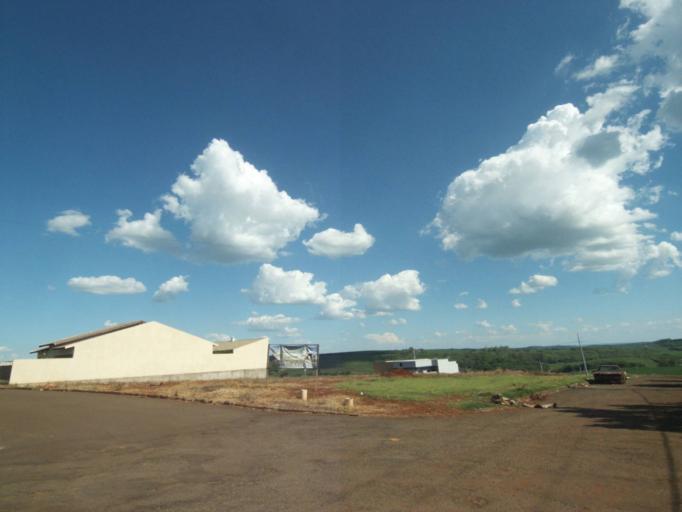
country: BR
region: Parana
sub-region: Sertanopolis
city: Sertanopolis
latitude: -23.0457
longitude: -50.8180
